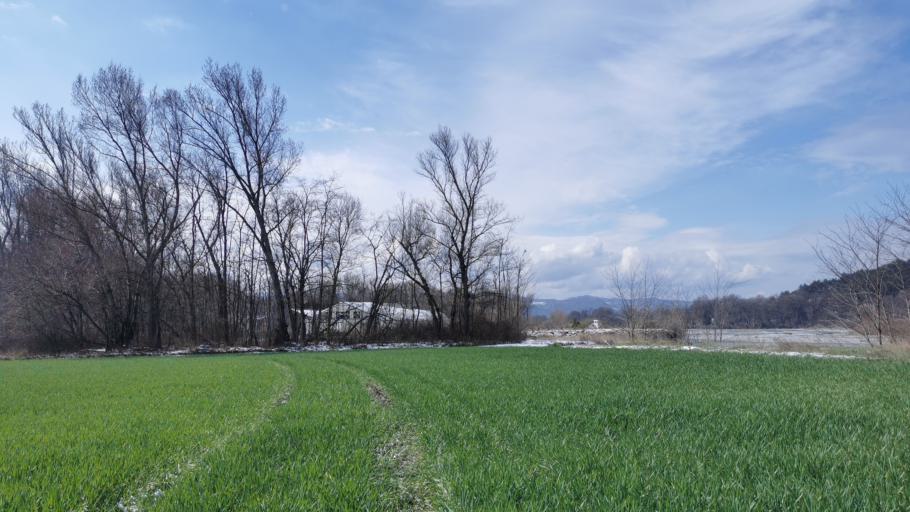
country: FR
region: Provence-Alpes-Cote d'Azur
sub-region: Departement des Alpes-de-Haute-Provence
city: Mallemoisson
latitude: 44.0570
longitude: 6.1654
